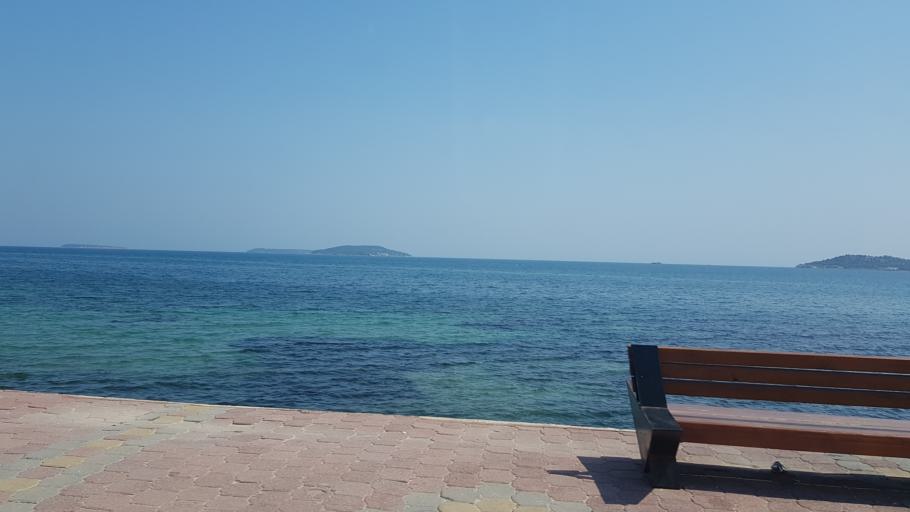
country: TR
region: Izmir
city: Urla
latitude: 38.3710
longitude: 26.7627
